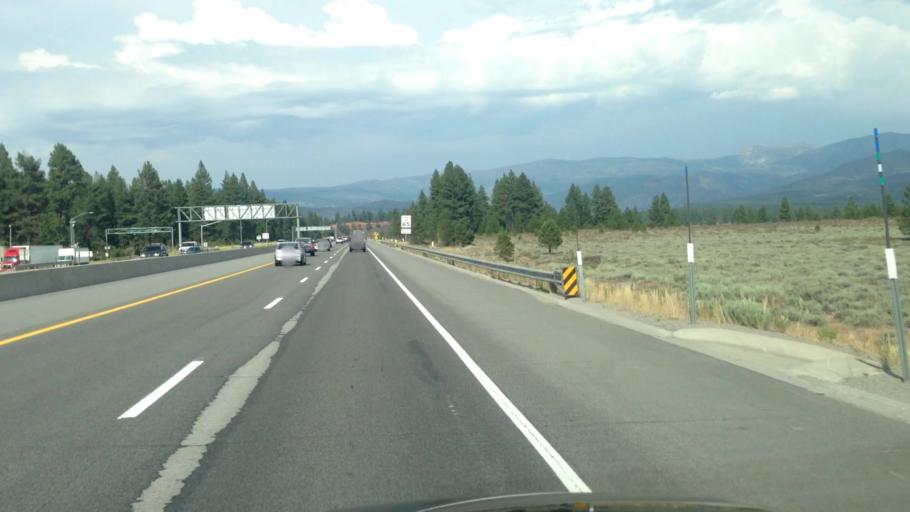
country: US
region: California
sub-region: Nevada County
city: Truckee
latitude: 39.3611
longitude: -120.1323
